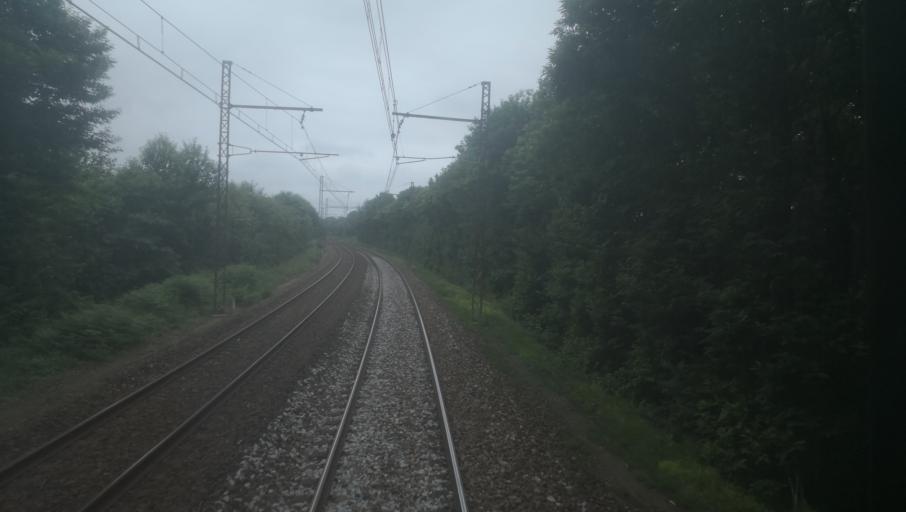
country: FR
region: Centre
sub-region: Departement de l'Indre
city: Chantome
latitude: 46.4609
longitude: 1.5416
